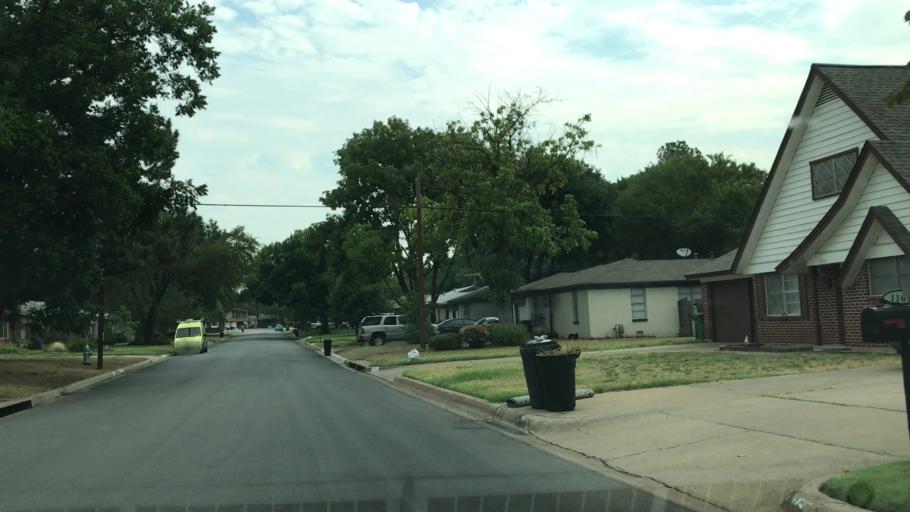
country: US
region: Texas
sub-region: Tarrant County
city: Hurst
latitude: 32.8317
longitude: -97.1698
